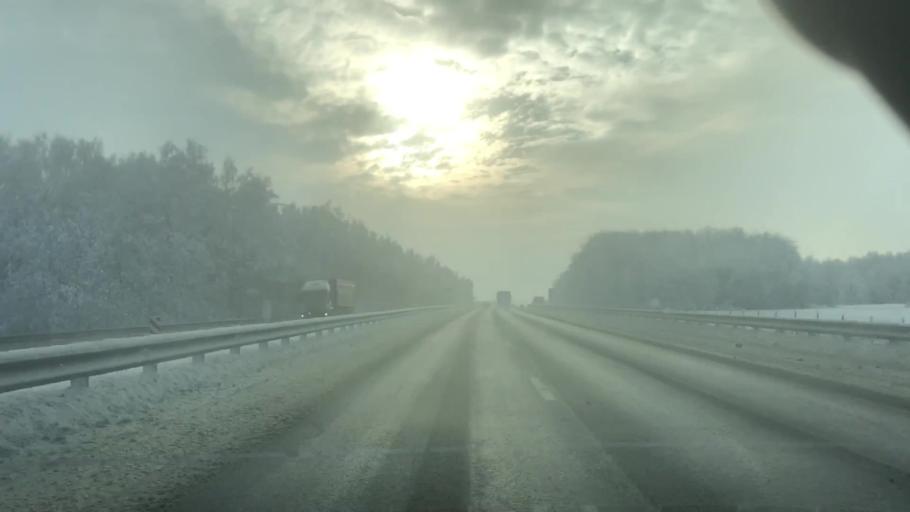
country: RU
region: Tula
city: Venev
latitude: 54.3826
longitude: 38.1550
